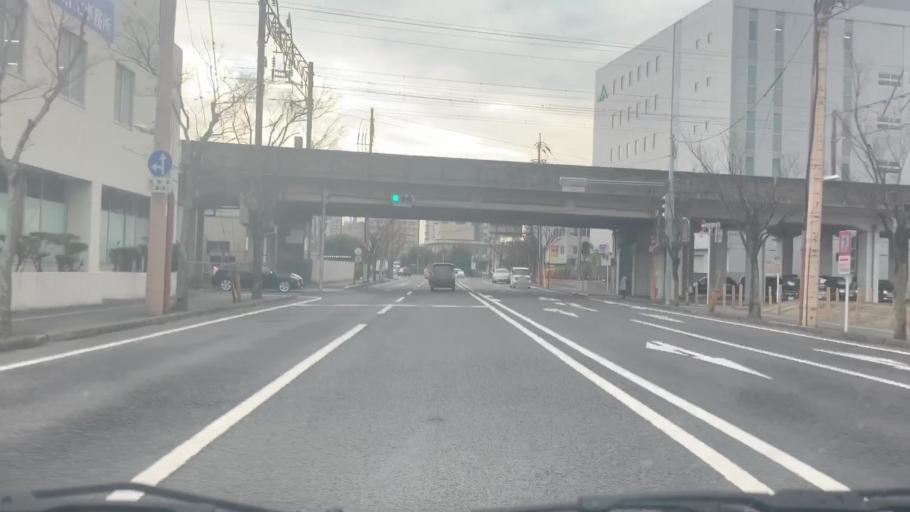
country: JP
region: Saga Prefecture
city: Saga-shi
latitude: 33.2654
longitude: 130.3020
